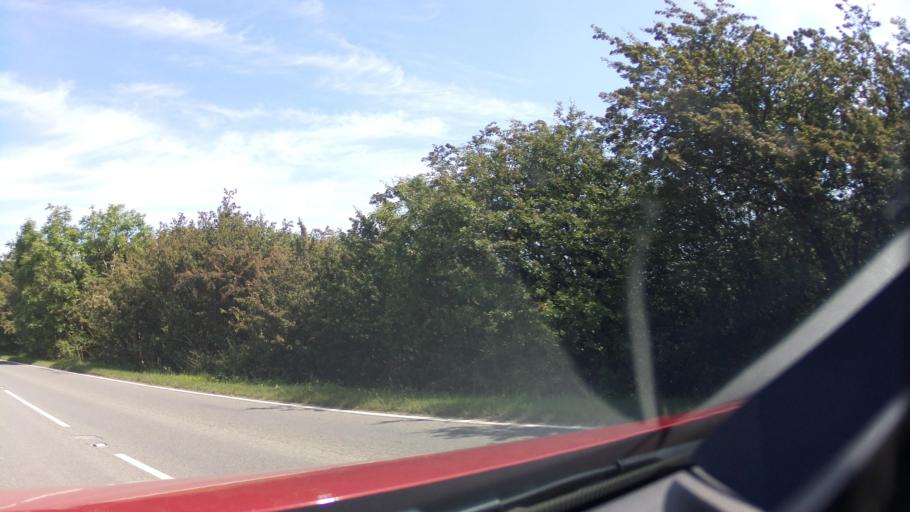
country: GB
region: England
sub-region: North Lincolnshire
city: Manton
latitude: 53.5025
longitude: -0.5820
